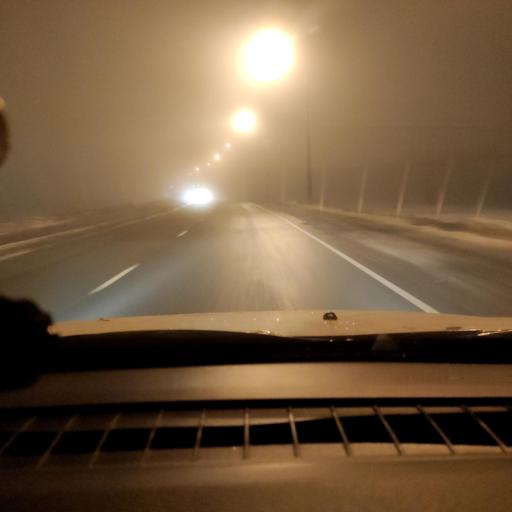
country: RU
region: Samara
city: Dubovyy Umet
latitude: 52.9671
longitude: 50.2815
